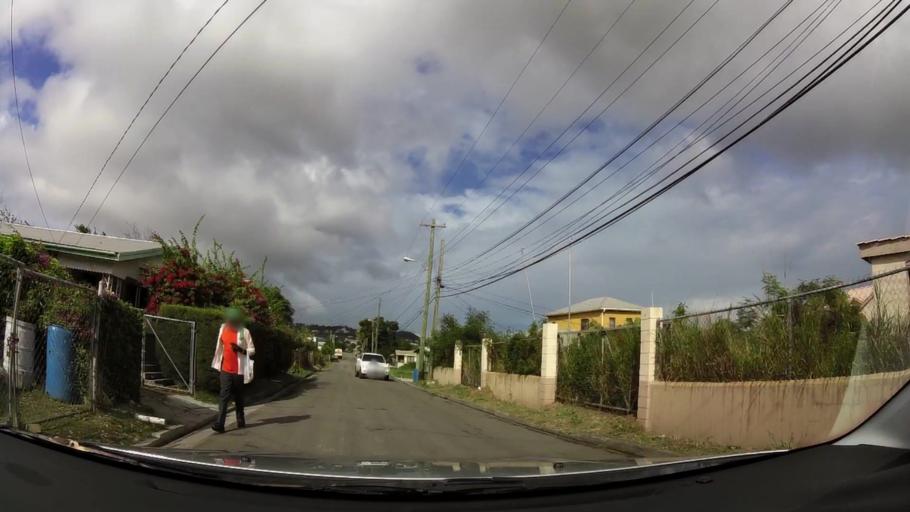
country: AG
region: Saint John
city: Saint John's
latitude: 17.1191
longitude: -61.8253
